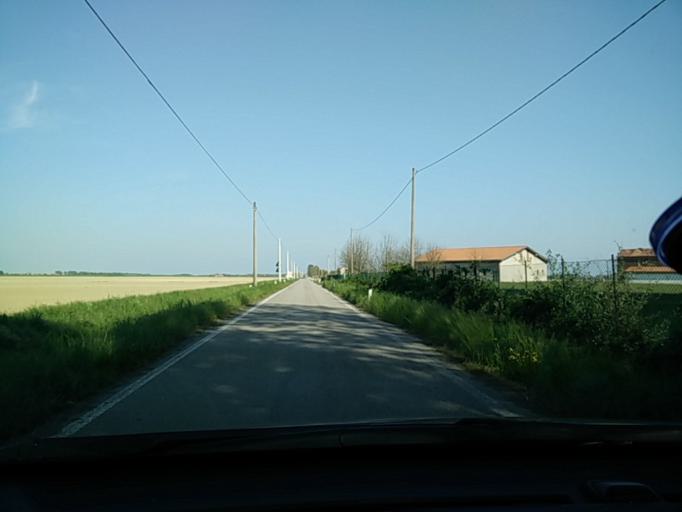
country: IT
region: Veneto
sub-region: Provincia di Venezia
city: Dese
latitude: 45.5298
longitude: 12.3228
